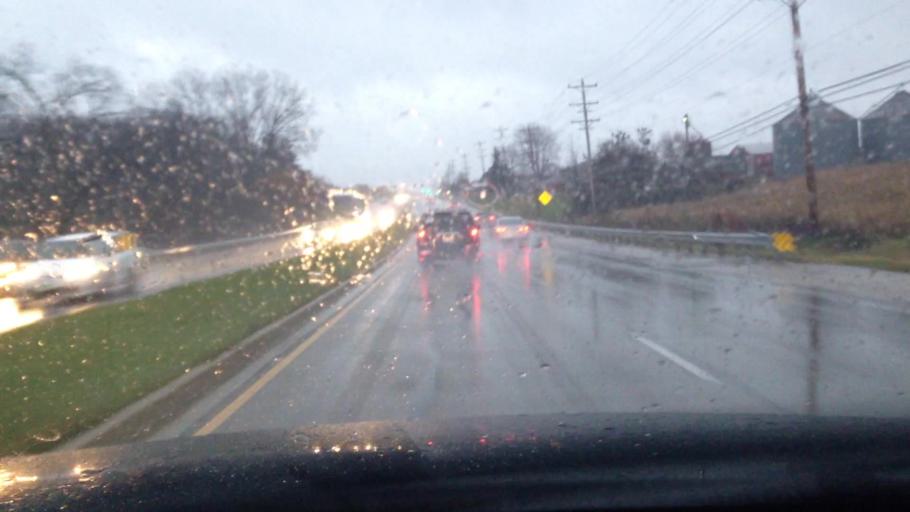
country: US
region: Illinois
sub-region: McHenry County
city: Lake in the Hills
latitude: 42.1756
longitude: -88.3774
